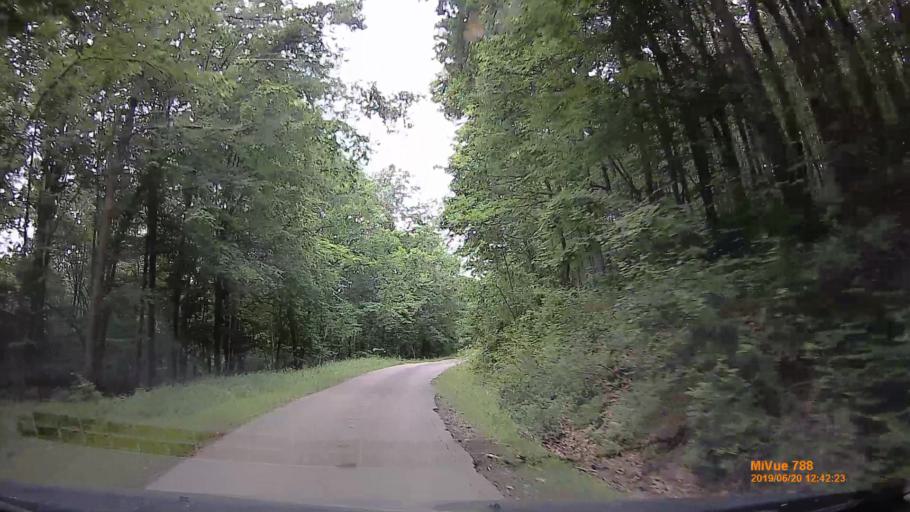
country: HU
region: Baranya
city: Hosszuheteny
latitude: 46.1978
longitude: 18.3607
